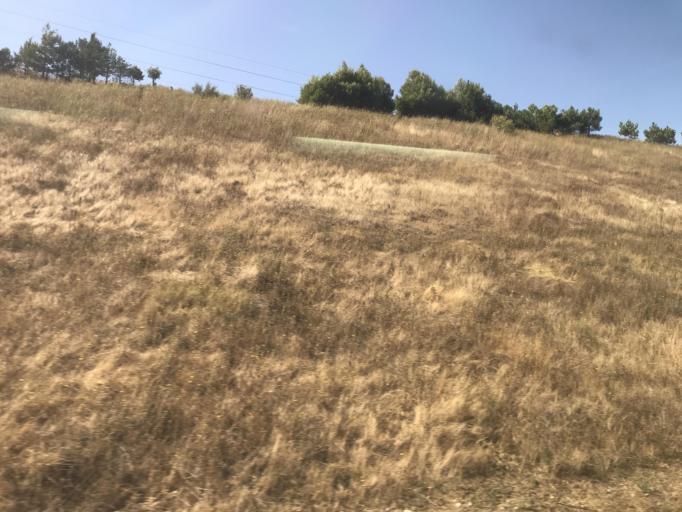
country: ES
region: Castille and Leon
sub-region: Provincia de Burgos
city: Hurones
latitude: 42.3743
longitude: -3.6407
